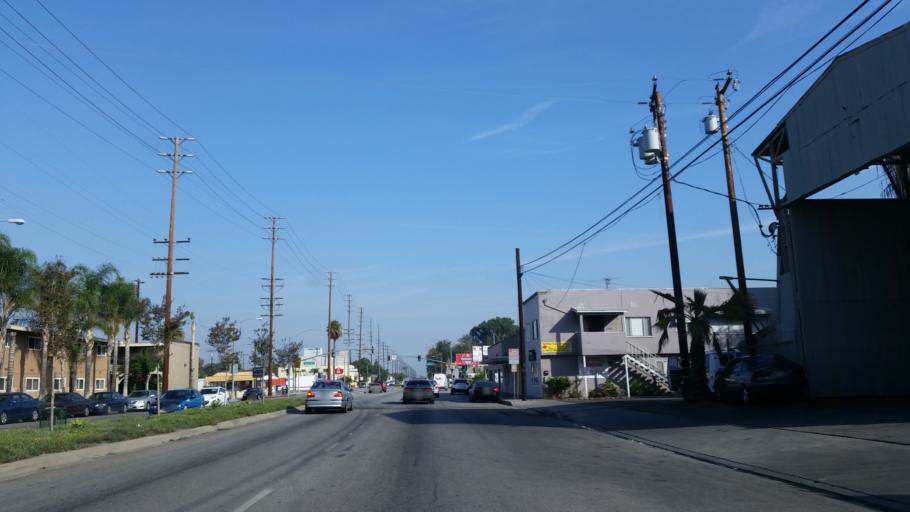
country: US
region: California
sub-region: Los Angeles County
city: Paramount
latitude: 33.8587
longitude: -118.1685
